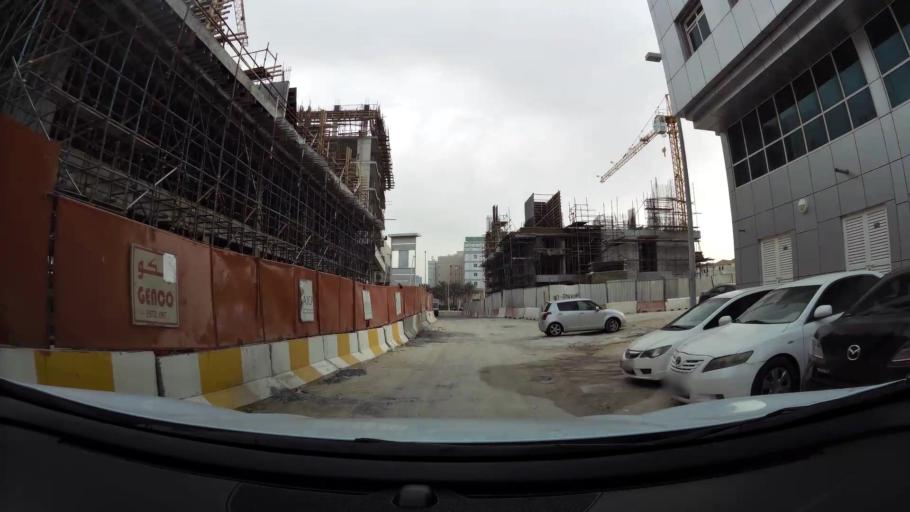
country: AE
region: Abu Dhabi
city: Abu Dhabi
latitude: 24.4766
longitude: 54.3816
